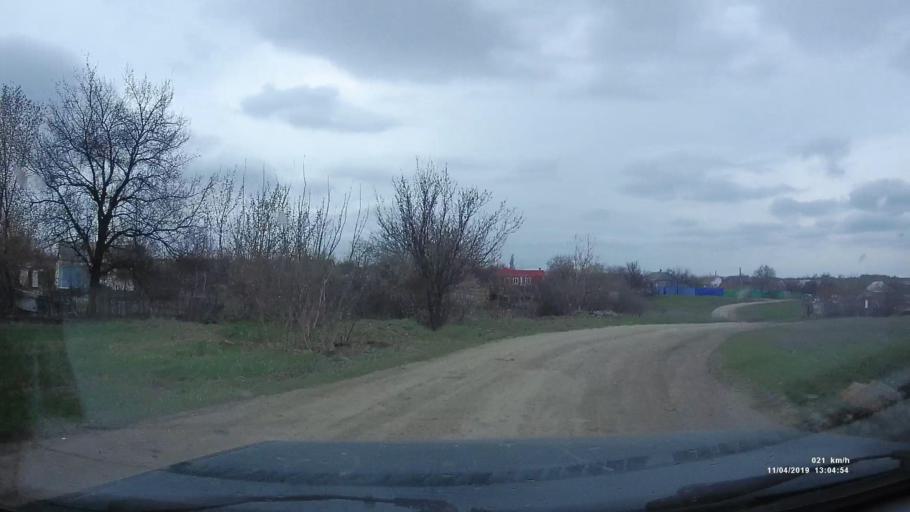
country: RU
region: Rostov
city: Staraya Stanitsa
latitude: 48.2871
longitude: 40.3447
